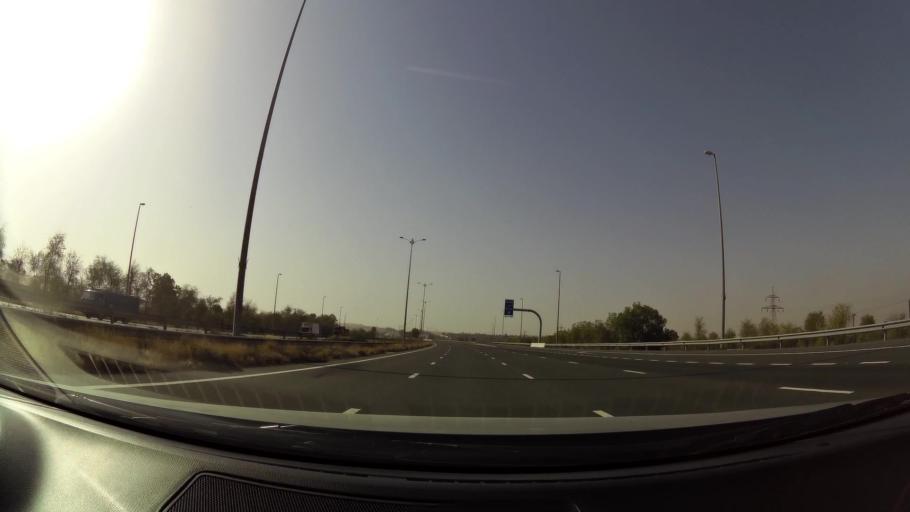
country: OM
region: Al Buraimi
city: Al Buraymi
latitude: 24.6442
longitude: 55.7067
